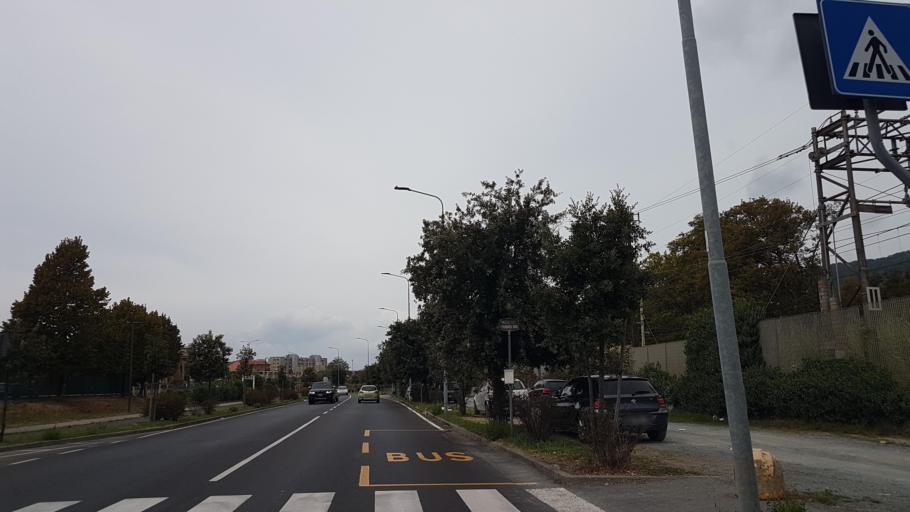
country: IT
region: Liguria
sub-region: Provincia di Genova
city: Sestri Levante
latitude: 44.2723
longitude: 9.4064
